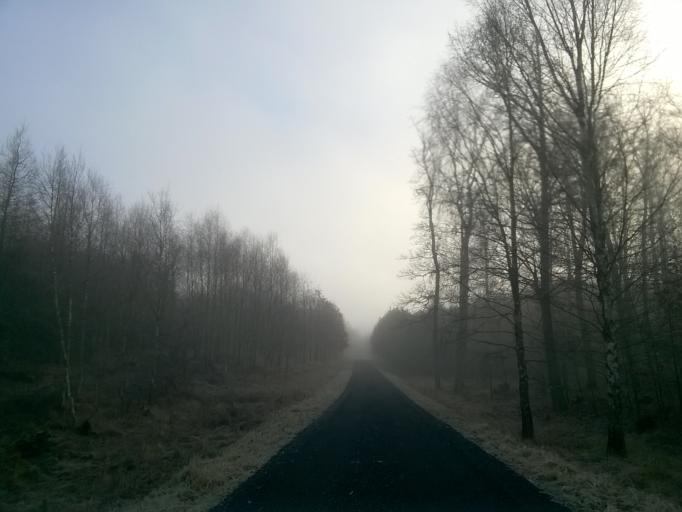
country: PL
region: Kujawsko-Pomorskie
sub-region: Powiat nakielski
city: Kcynia
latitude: 53.0483
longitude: 17.4862
